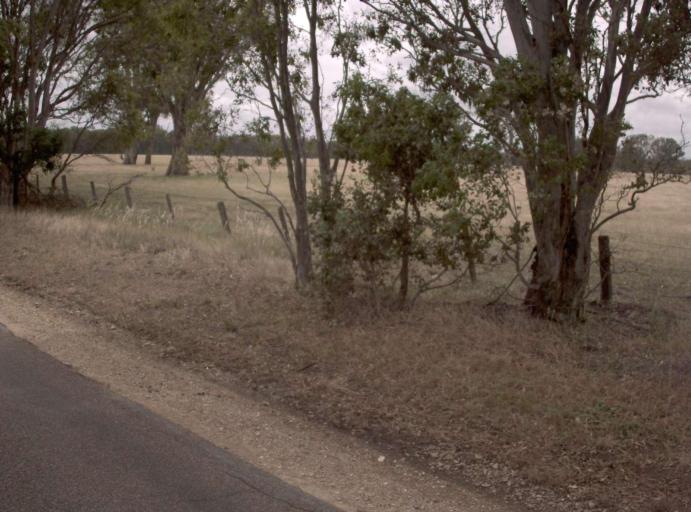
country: AU
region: Victoria
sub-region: Wellington
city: Sale
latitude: -37.8760
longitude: 147.0662
